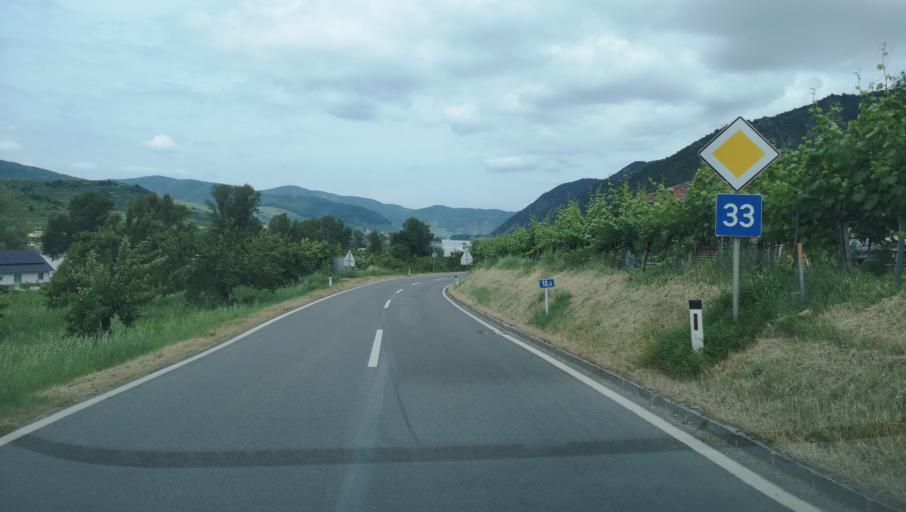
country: AT
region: Lower Austria
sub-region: Politischer Bezirk Krems
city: Spitz
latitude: 48.3661
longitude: 15.4385
